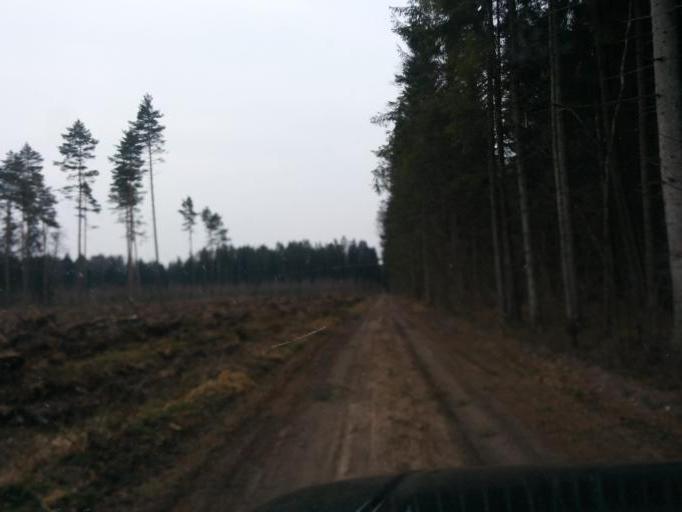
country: LV
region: Ikskile
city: Ikskile
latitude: 56.8094
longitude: 24.4817
